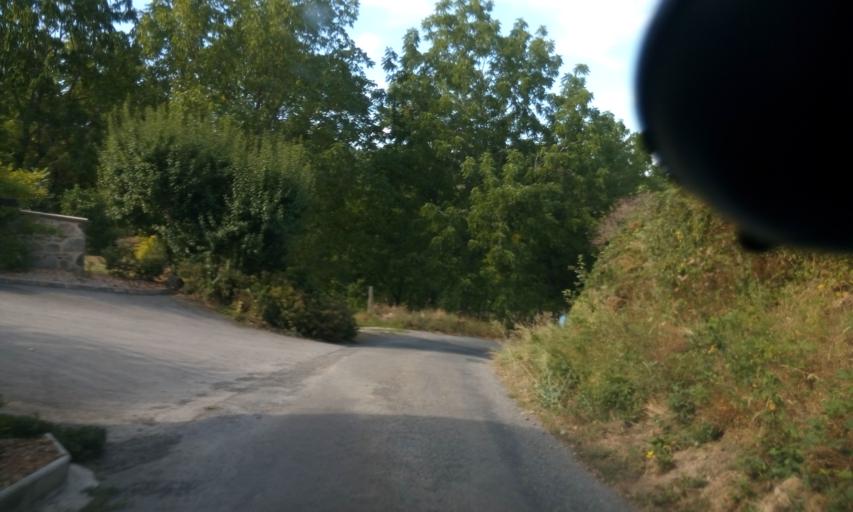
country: FR
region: Rhone-Alpes
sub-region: Departement du Rhone
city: Cublize
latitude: 45.9854
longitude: 4.3925
